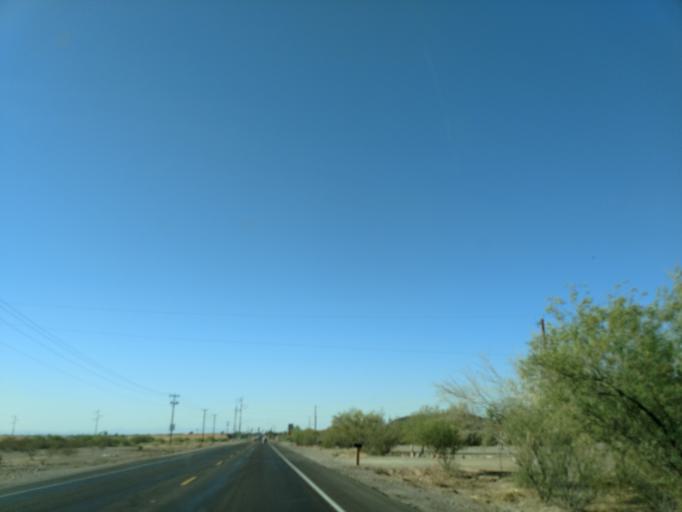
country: US
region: Arizona
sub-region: Maricopa County
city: Laveen
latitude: 33.3205
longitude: -112.1691
